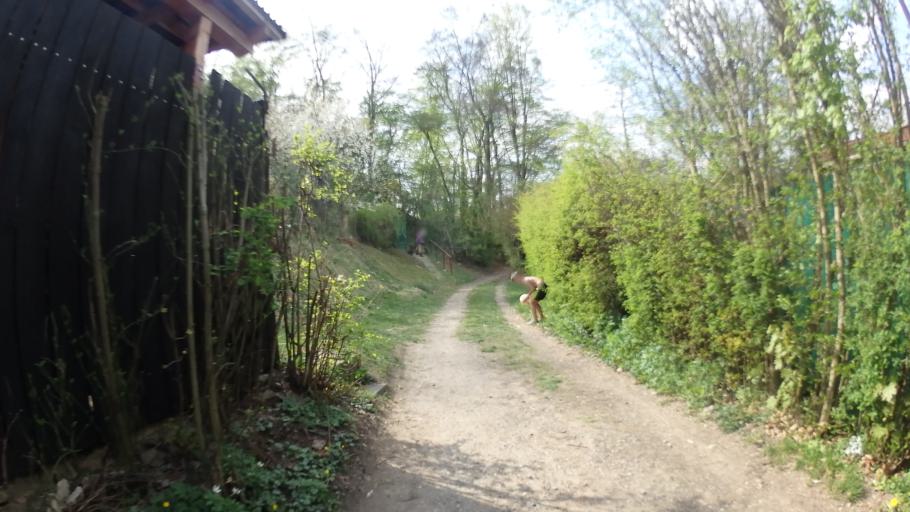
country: CZ
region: South Moravian
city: Ostopovice
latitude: 49.2177
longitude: 16.5473
